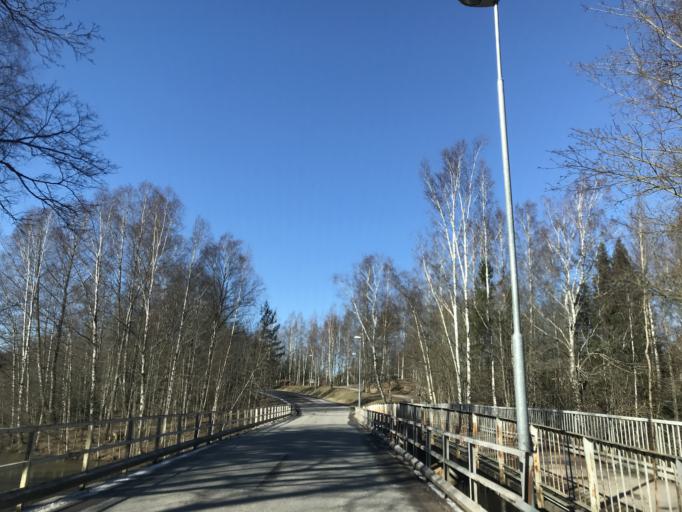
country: FI
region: Uusimaa
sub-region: Raaseporin
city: Karis
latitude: 60.0768
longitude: 23.6795
